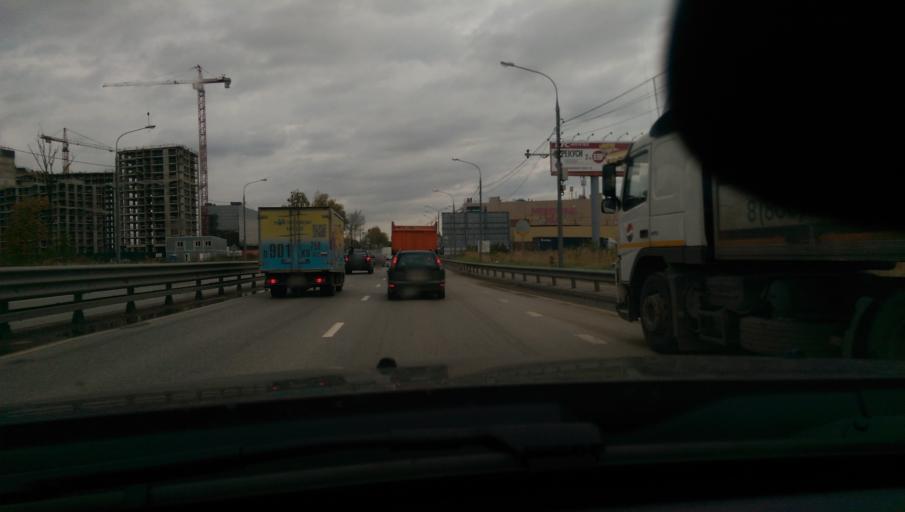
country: RU
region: Moscow
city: Vatutino
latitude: 55.9188
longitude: 37.6660
